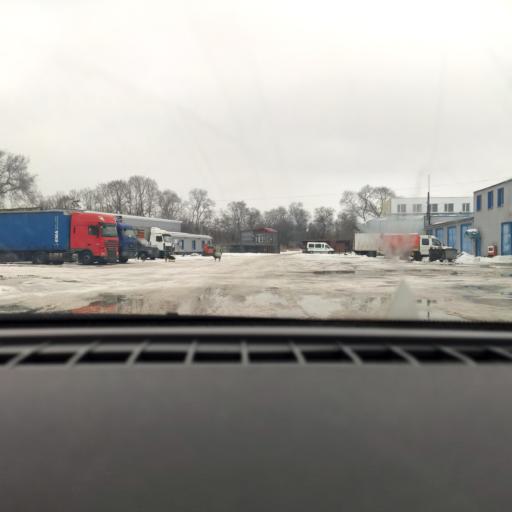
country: RU
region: Voronezj
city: Maslovka
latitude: 51.6370
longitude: 39.3019
